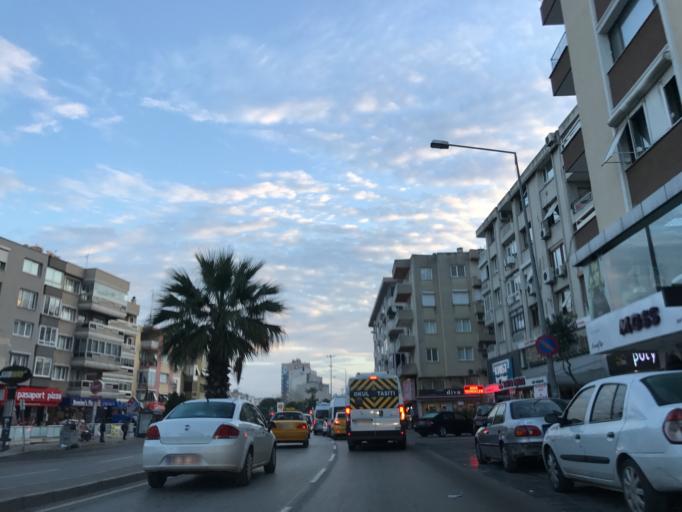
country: TR
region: Izmir
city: Izmir
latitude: 38.4013
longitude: 27.1150
